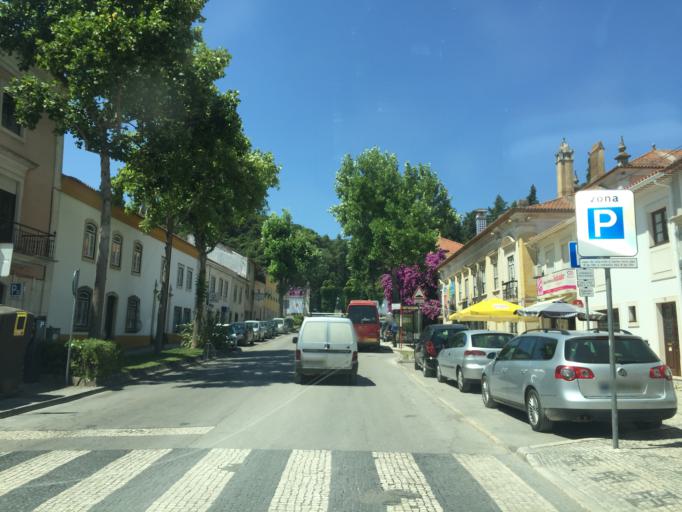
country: PT
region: Santarem
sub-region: Tomar
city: Tomar
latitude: 39.6018
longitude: -8.4146
